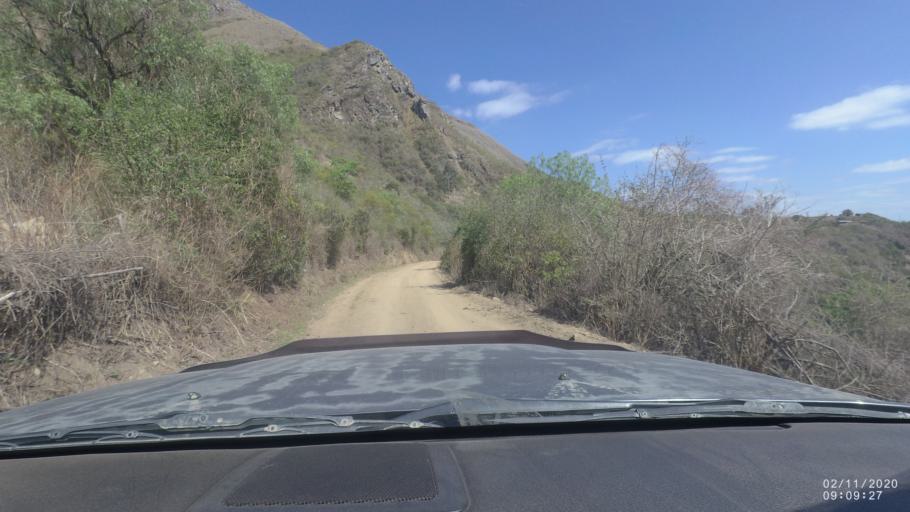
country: BO
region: Chuquisaca
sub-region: Provincia Zudanez
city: Mojocoya
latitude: -18.5212
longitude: -64.5650
